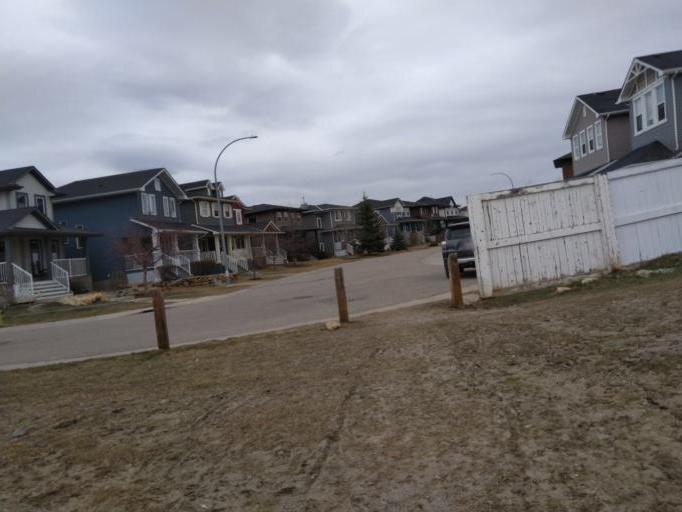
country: CA
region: Alberta
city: Calgary
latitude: 51.1686
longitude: -114.1090
